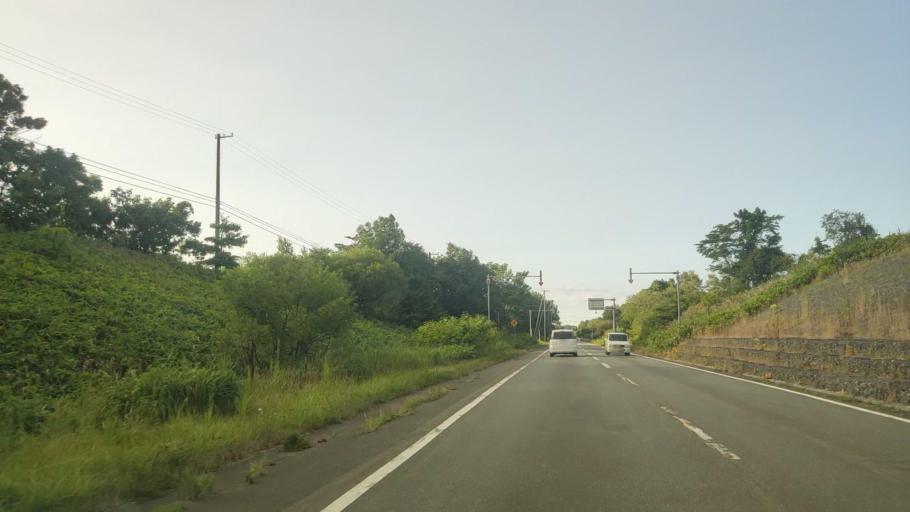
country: JP
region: Hokkaido
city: Makubetsu
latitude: 45.0602
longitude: 141.7484
